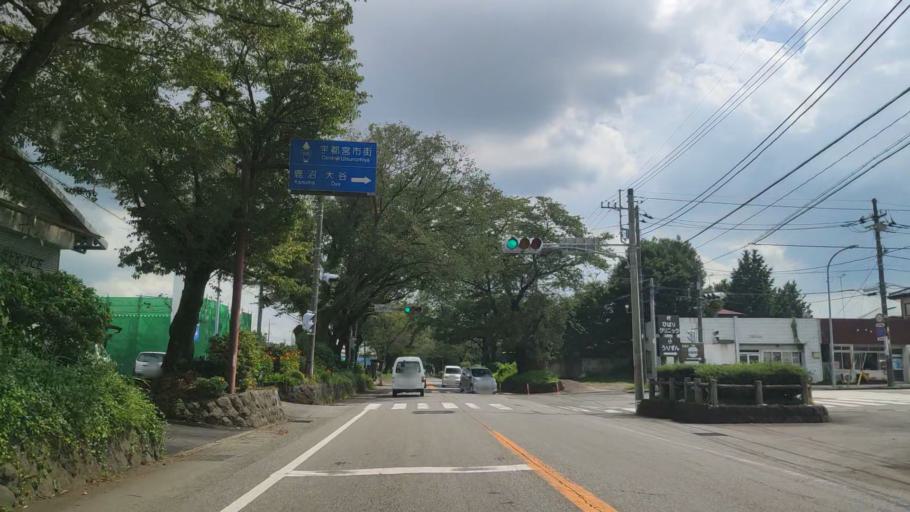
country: JP
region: Tochigi
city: Utsunomiya-shi
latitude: 36.6414
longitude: 139.8480
